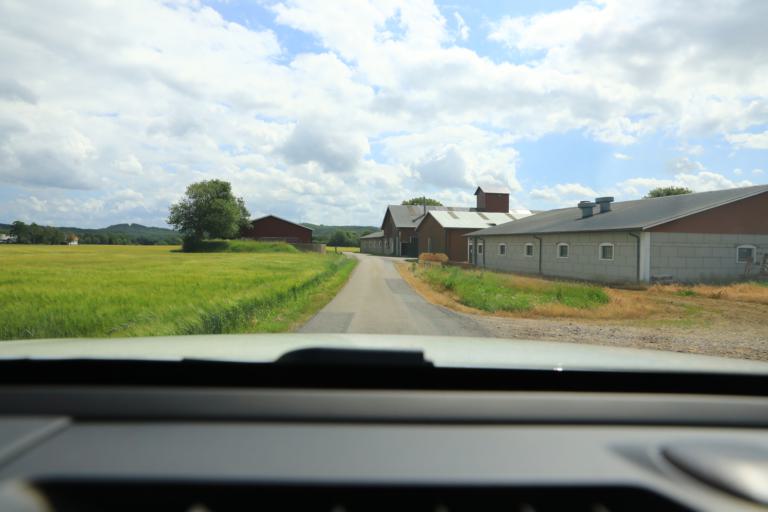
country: SE
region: Halland
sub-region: Varbergs Kommun
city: Tvaaker
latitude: 57.0848
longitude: 12.3932
